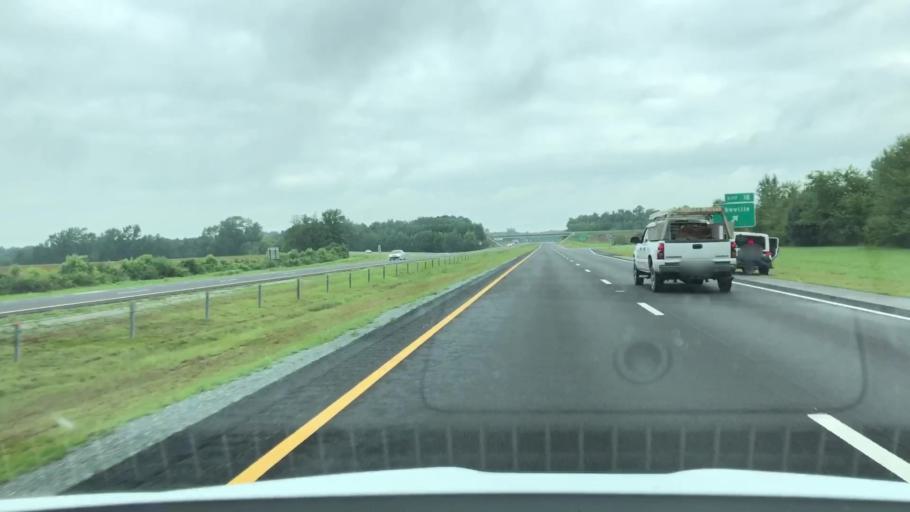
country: US
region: North Carolina
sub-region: Wayne County
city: Fremont
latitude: 35.4904
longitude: -77.9939
